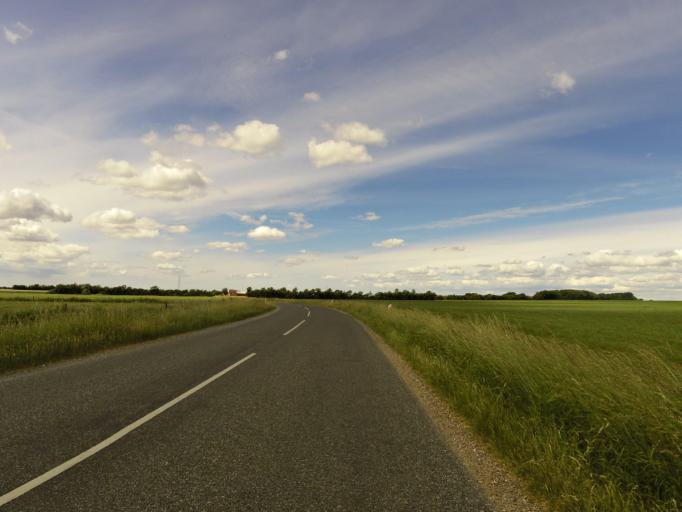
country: DK
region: South Denmark
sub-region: Esbjerg Kommune
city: Ribe
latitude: 55.2630
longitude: 8.8187
